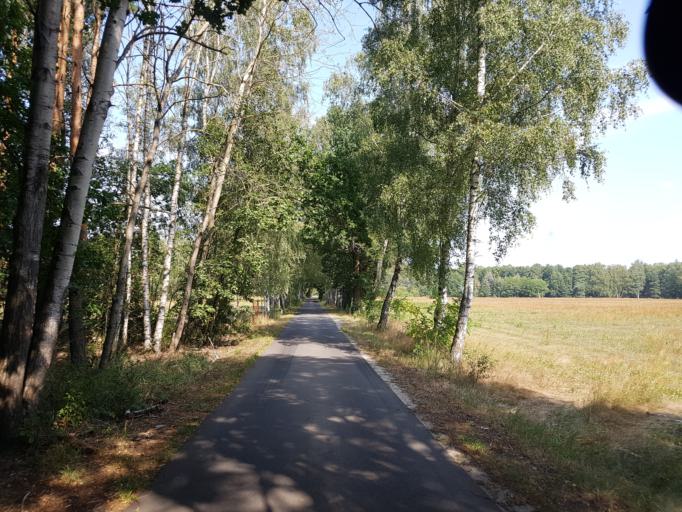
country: DE
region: Brandenburg
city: Finsterwalde
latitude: 51.6564
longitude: 13.7622
